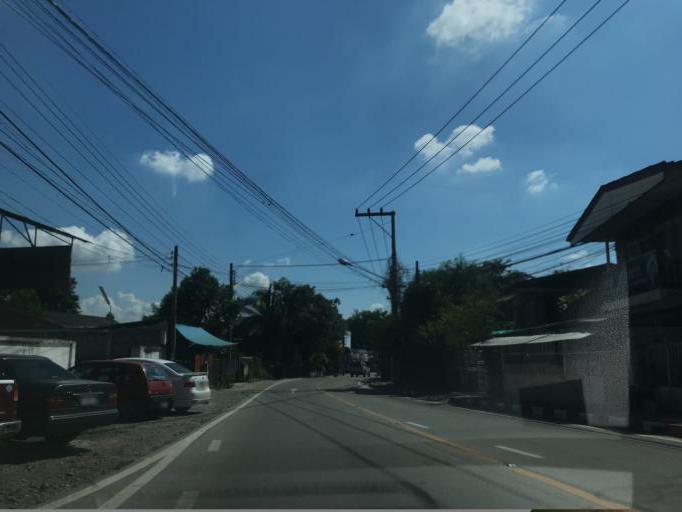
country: TH
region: Chiang Mai
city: Chiang Mai
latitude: 18.7989
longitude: 98.9901
